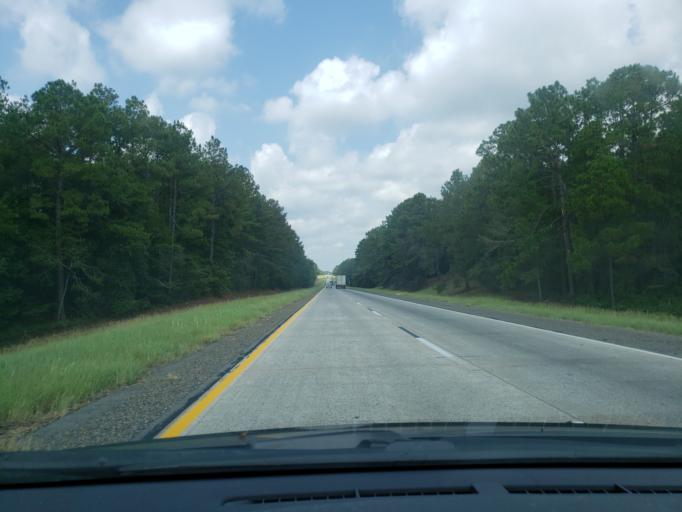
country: US
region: Georgia
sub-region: Treutlen County
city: Soperton
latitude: 32.4280
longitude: -82.5598
